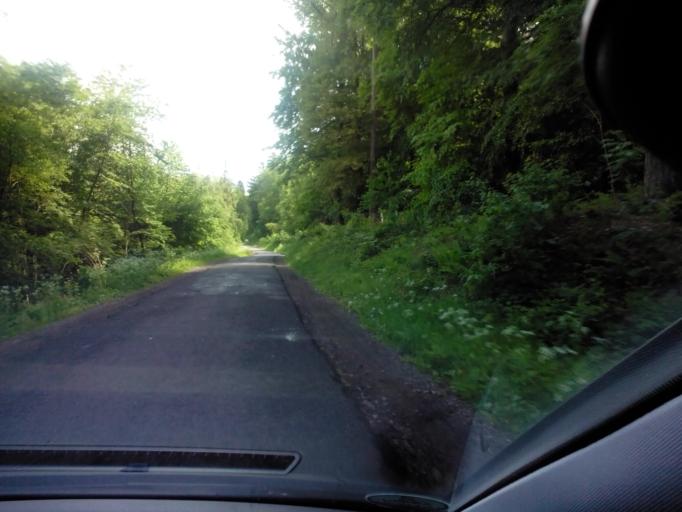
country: DE
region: Saarland
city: Schmelz
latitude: 49.3904
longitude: 6.8590
